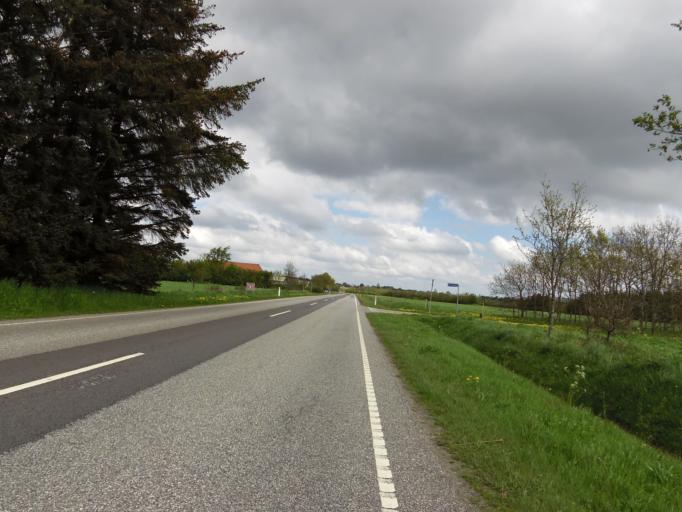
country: DK
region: South Denmark
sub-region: Haderslev Kommune
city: Gram
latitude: 55.2656
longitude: 8.9984
